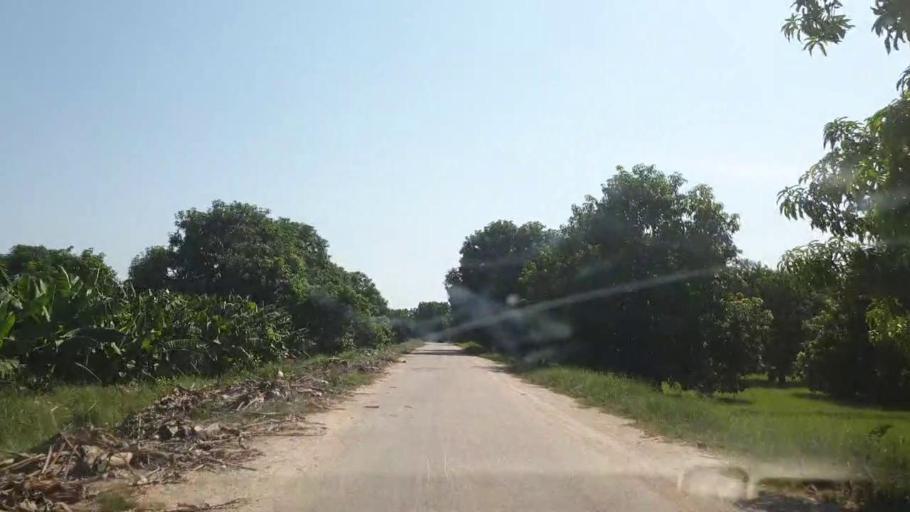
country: PK
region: Sindh
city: Tando Jam
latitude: 25.4078
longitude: 68.5821
